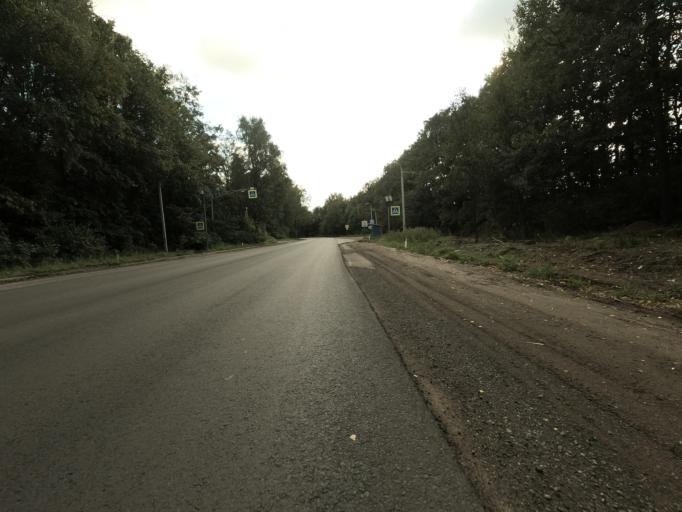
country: RU
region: Leningrad
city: Koltushi
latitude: 59.9452
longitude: 30.6569
